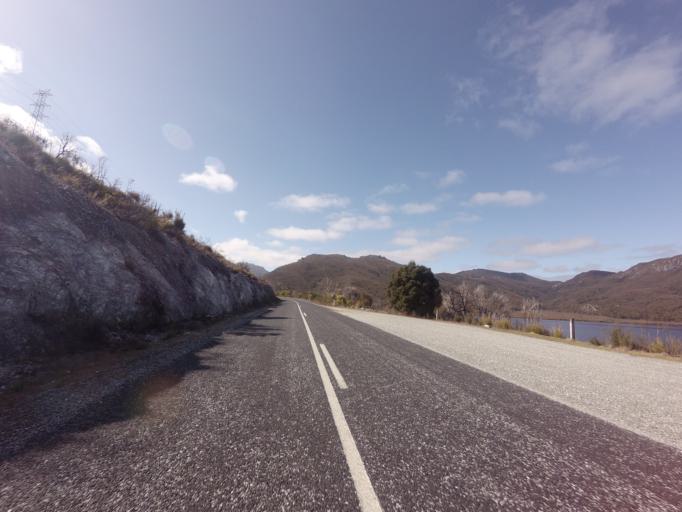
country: AU
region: Tasmania
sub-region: Huon Valley
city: Geeveston
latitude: -42.8462
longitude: 146.1691
